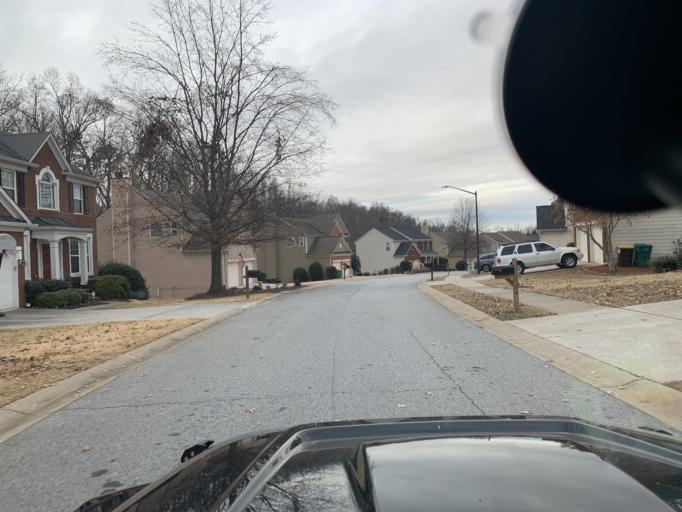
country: US
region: Georgia
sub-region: Cherokee County
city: Woodstock
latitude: 34.0944
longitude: -84.4607
